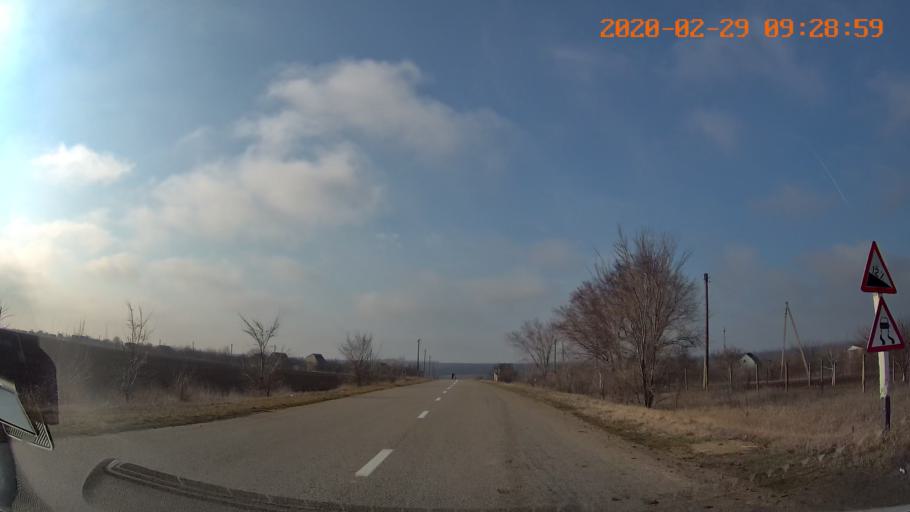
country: UA
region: Odessa
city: Lymanske
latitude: 46.6828
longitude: 29.9245
